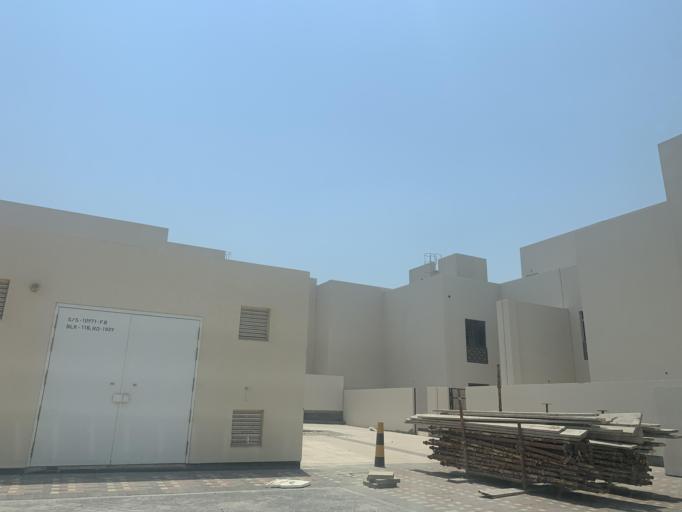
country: BH
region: Muharraq
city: Al Hadd
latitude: 26.2417
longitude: 50.6632
